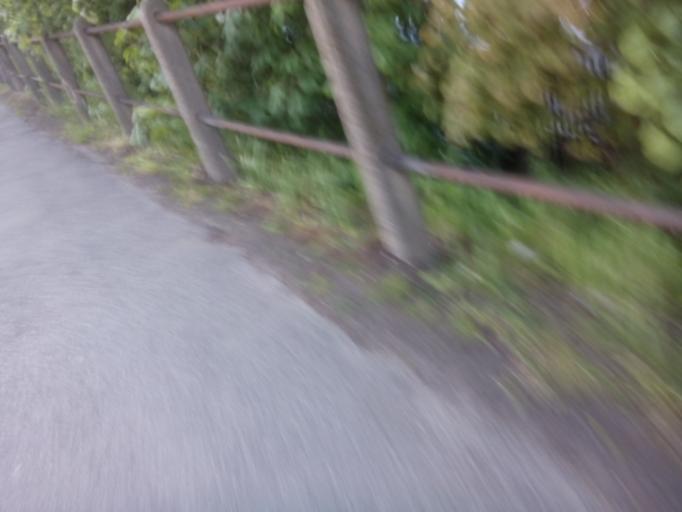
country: GB
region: England
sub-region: County Durham
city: Durham
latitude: 54.7785
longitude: -1.5792
